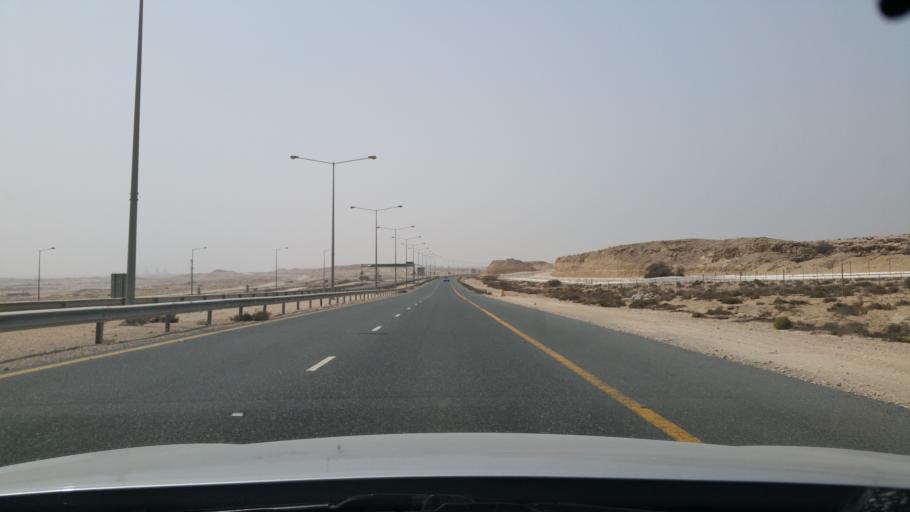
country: QA
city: Umm Bab
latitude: 25.2788
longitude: 50.7918
